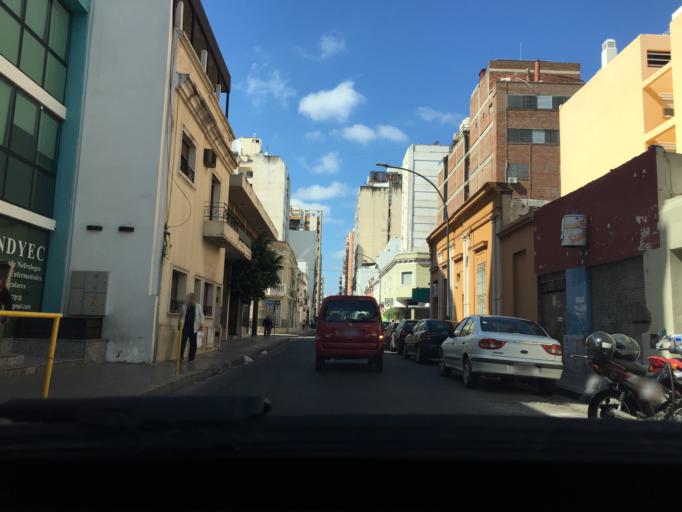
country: AR
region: Cordoba
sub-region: Departamento de Capital
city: Cordoba
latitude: -31.4090
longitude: -64.1934
